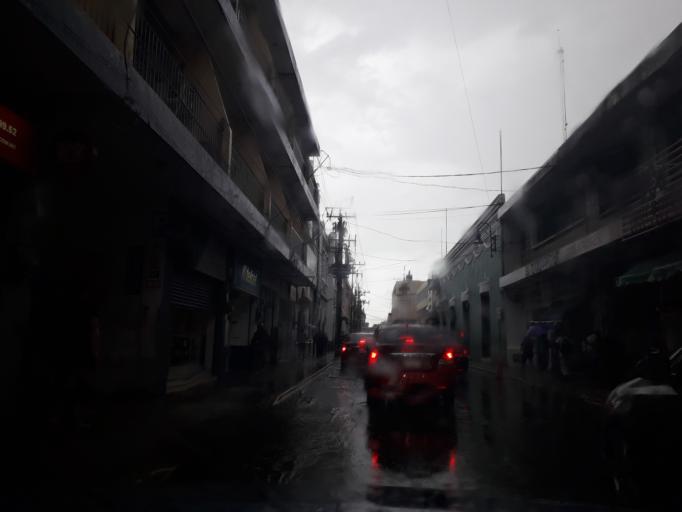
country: MX
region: Yucatan
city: Merida
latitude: 20.9641
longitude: -89.6237
